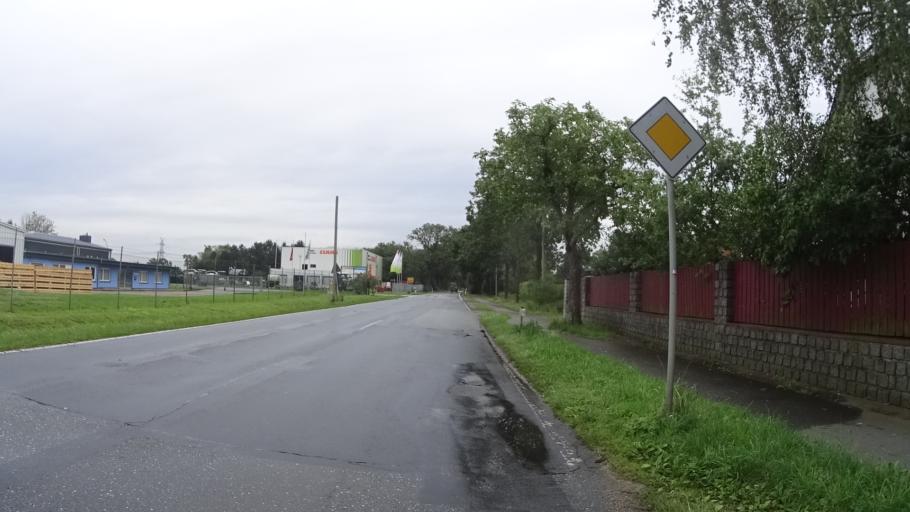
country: DE
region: Schleswig-Holstein
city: Alveslohe
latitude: 53.7895
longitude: 9.9246
